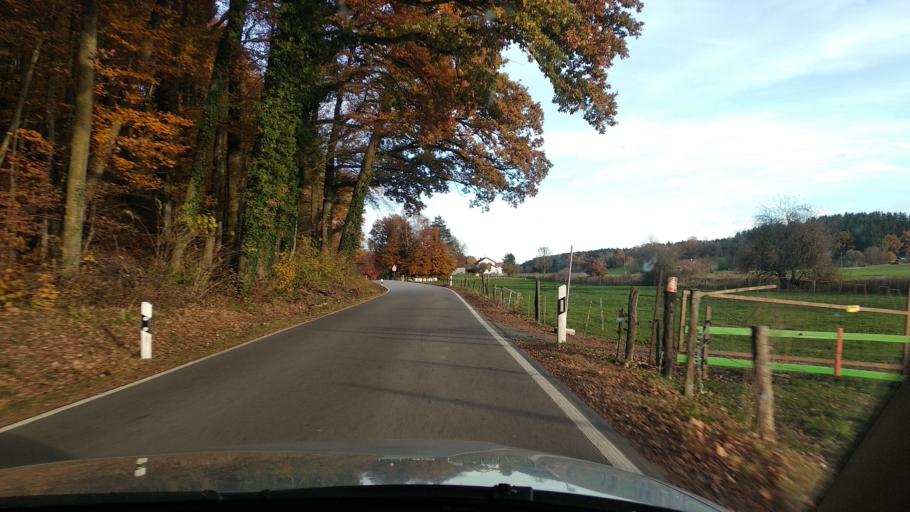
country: DE
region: Bavaria
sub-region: Upper Bavaria
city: Bruck
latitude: 48.0398
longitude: 11.9195
